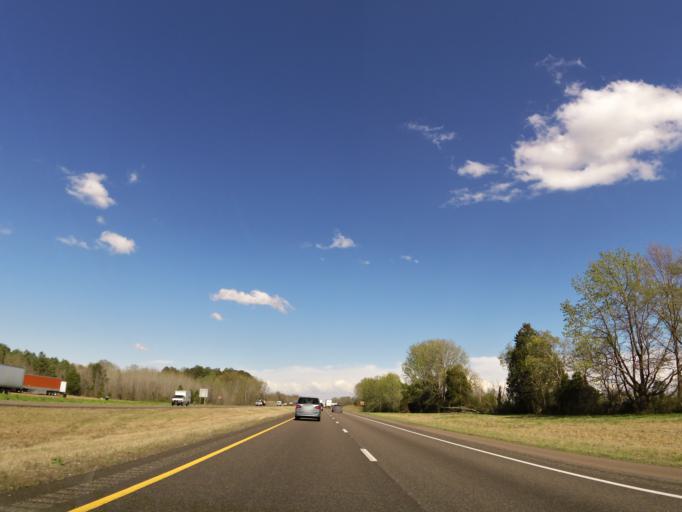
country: US
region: Tennessee
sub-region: Henderson County
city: Lexington
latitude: 35.7596
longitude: -88.4909
